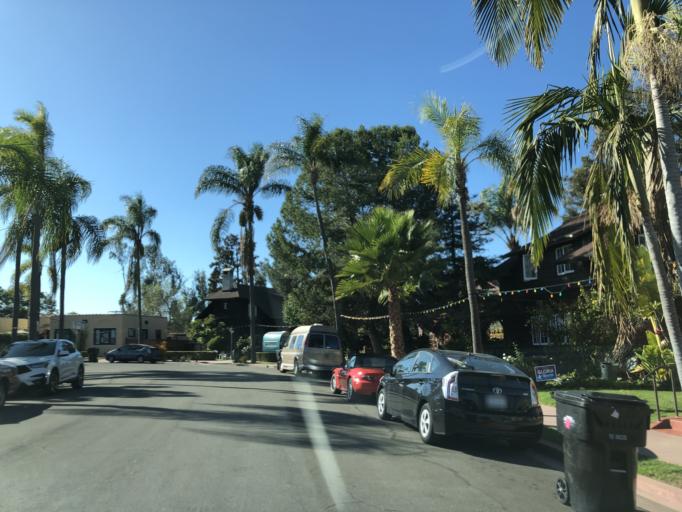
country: US
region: California
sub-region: San Diego County
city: San Diego
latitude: 32.7329
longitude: -117.1283
